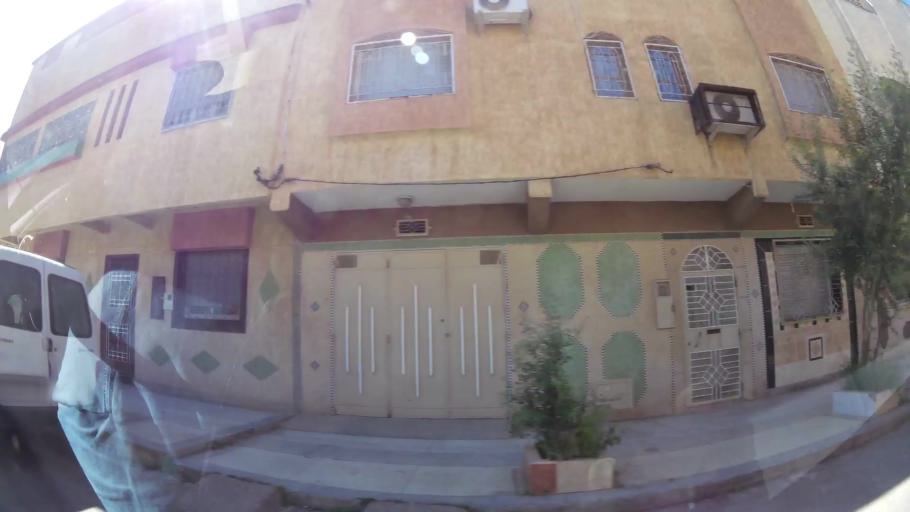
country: MA
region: Oriental
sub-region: Oujda-Angad
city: Oujda
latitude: 34.6697
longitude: -1.9272
